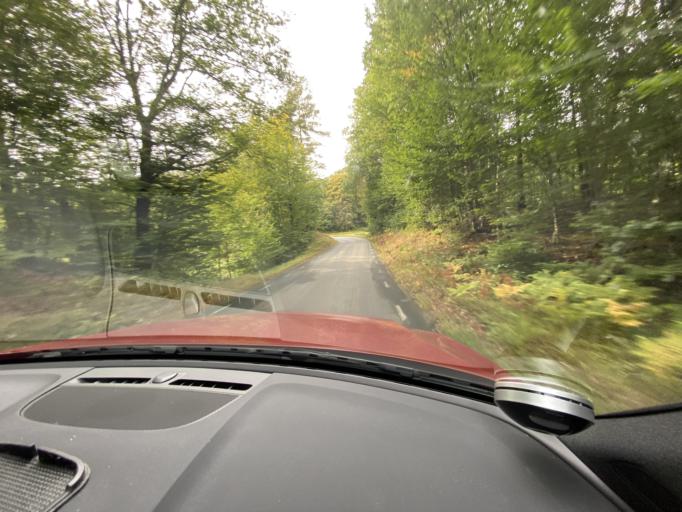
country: SE
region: Skane
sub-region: Hassleholms Kommun
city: Bjarnum
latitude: 56.3515
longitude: 13.7074
